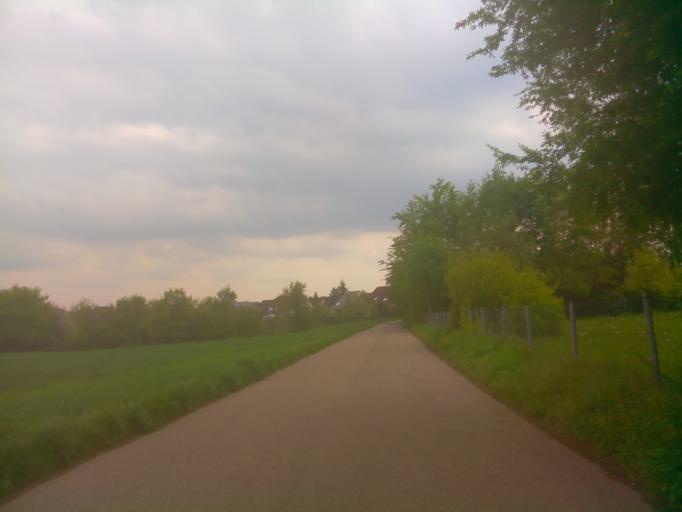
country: DE
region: Baden-Wuerttemberg
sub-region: Karlsruhe Region
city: Plankstadt
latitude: 49.3993
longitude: 8.5914
